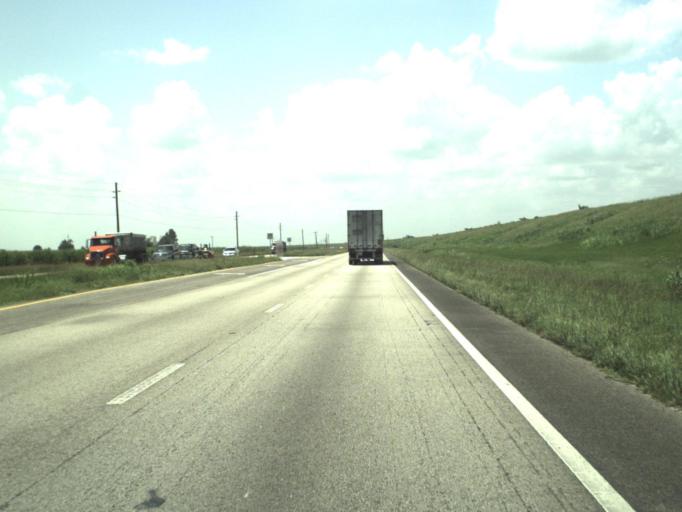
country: US
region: Florida
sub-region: Palm Beach County
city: South Bay
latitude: 26.6906
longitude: -80.7664
